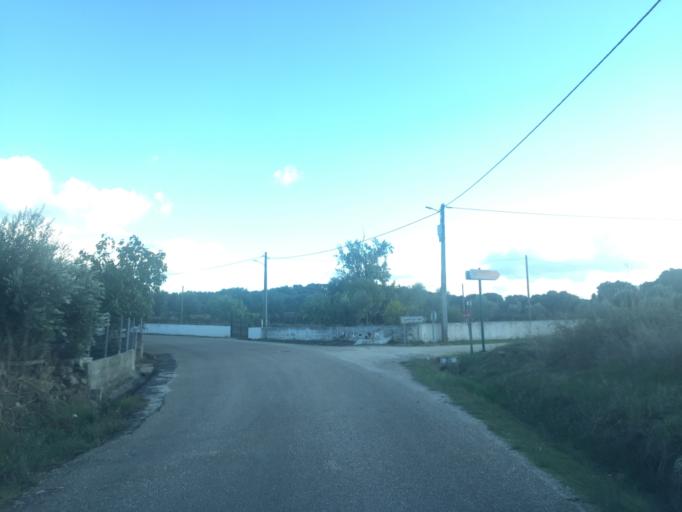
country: PT
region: Portalegre
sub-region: Alter do Chao
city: Alter do Chao
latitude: 39.1873
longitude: -7.6284
